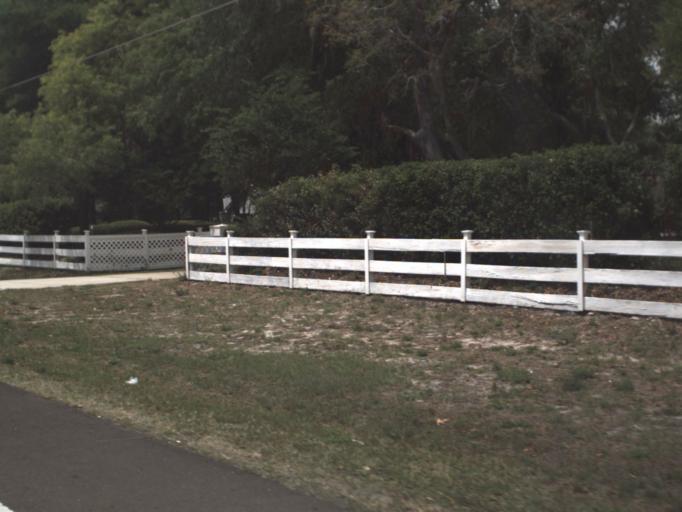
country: US
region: Florida
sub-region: Lake County
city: Mount Dora
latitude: 28.8359
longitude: -81.6382
